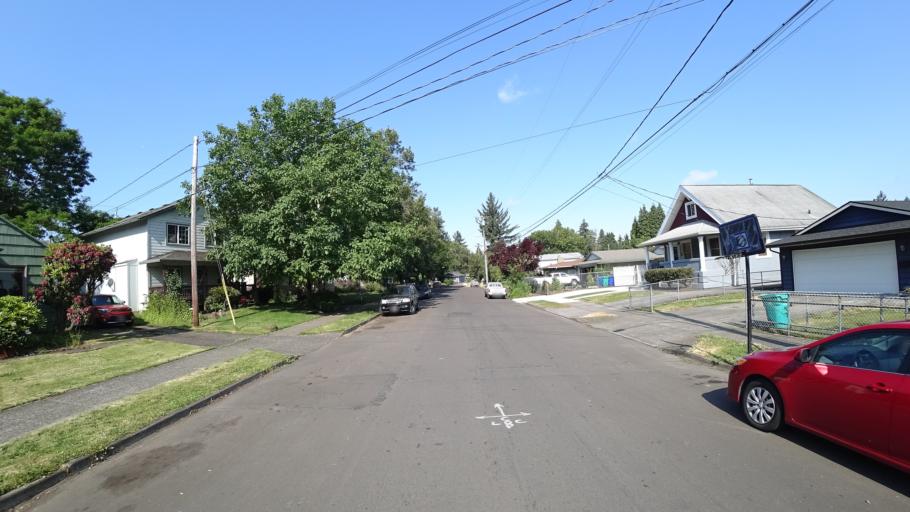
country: US
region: Oregon
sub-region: Washington County
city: West Haven
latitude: 45.5945
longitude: -122.7356
